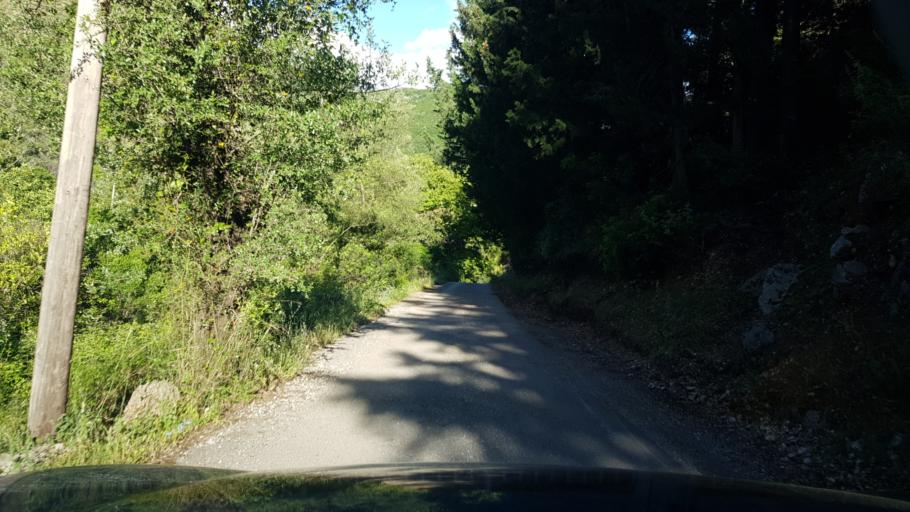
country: GR
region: Ionian Islands
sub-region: Lefkada
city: Nidri
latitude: 38.7226
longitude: 20.6915
